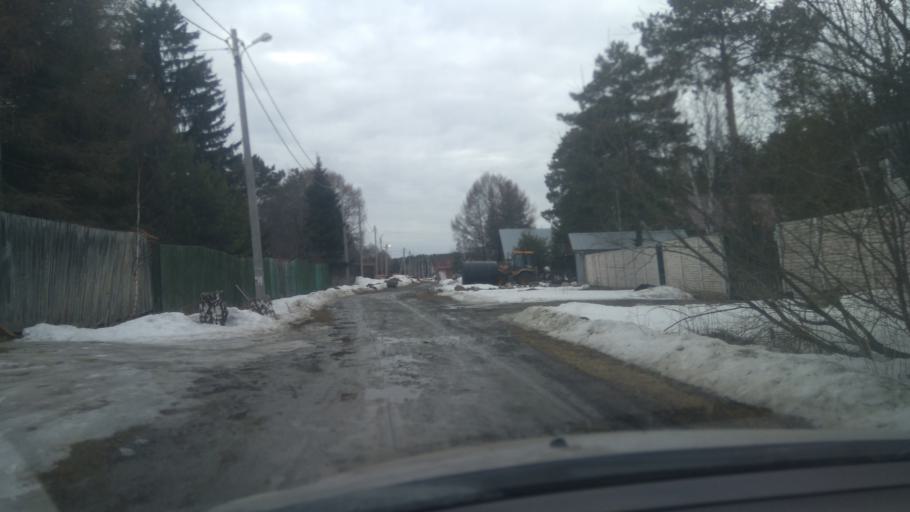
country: RU
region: Sverdlovsk
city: Severka
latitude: 56.8538
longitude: 60.3845
